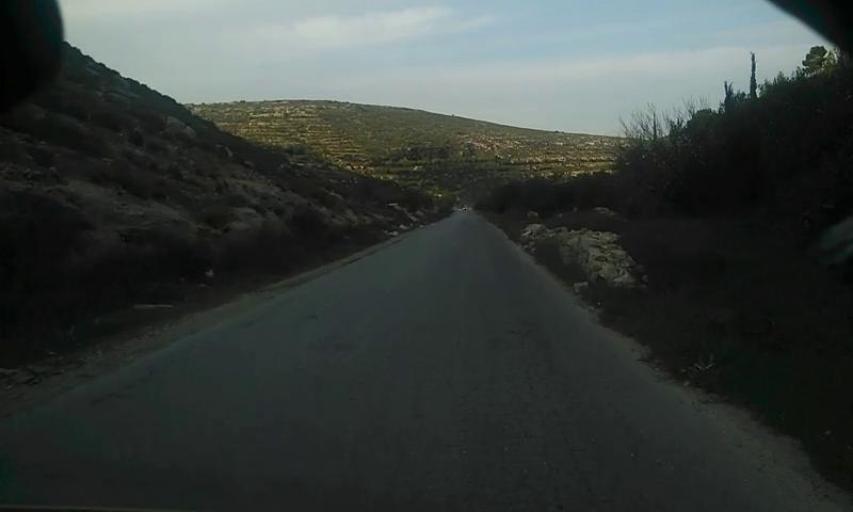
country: PS
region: West Bank
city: Bayt Fajjar
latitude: 31.5985
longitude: 35.1792
